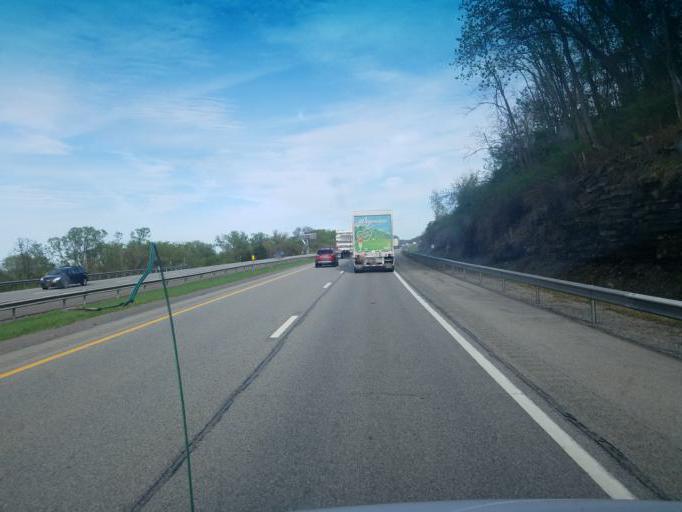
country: US
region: New York
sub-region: Herkimer County
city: Herkimer
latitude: 43.0132
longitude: -74.9245
